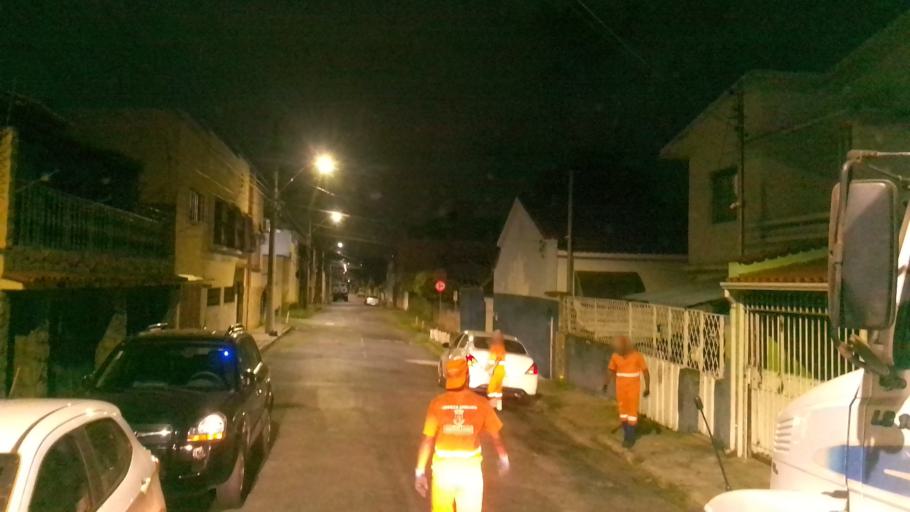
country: BR
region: Minas Gerais
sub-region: Belo Horizonte
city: Belo Horizonte
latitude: -19.9121
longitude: -43.9672
